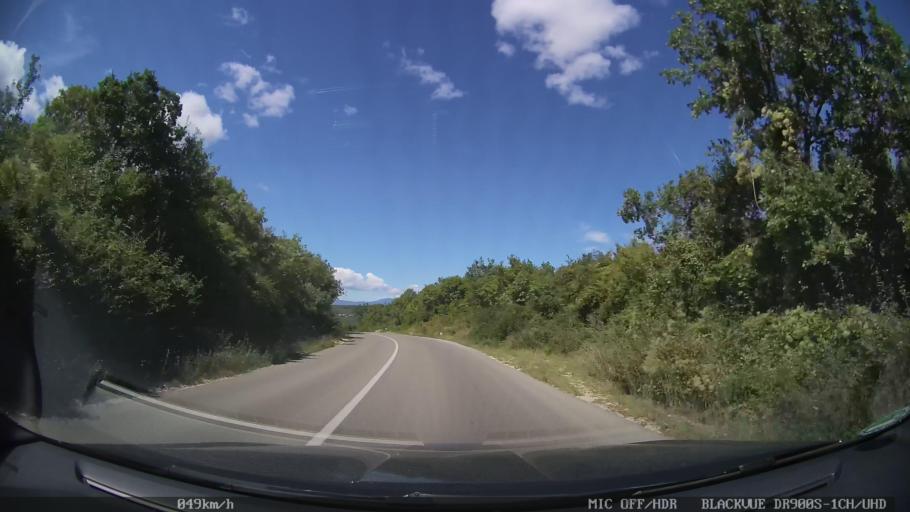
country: HR
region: Primorsko-Goranska
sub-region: Grad Krk
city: Krk
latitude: 45.0485
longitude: 14.5093
